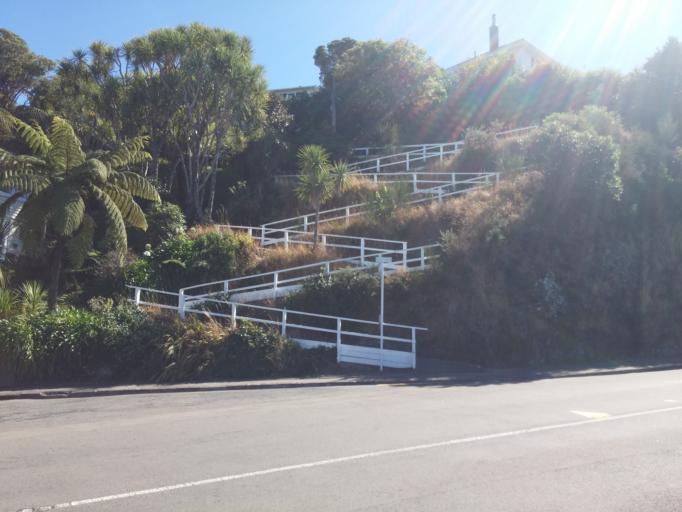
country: NZ
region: Wellington
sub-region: Wellington City
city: Kelburn
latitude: -41.2840
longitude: 174.7564
